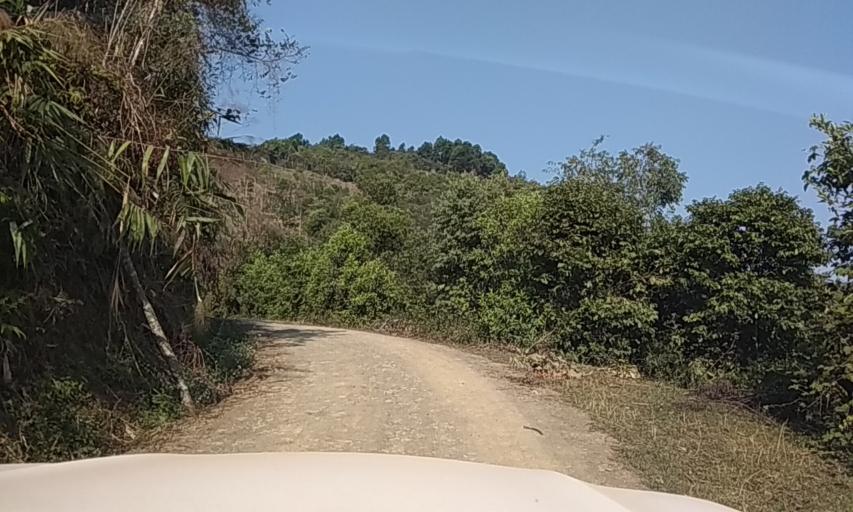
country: LA
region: Phongsali
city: Phongsali
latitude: 21.6953
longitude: 102.0845
